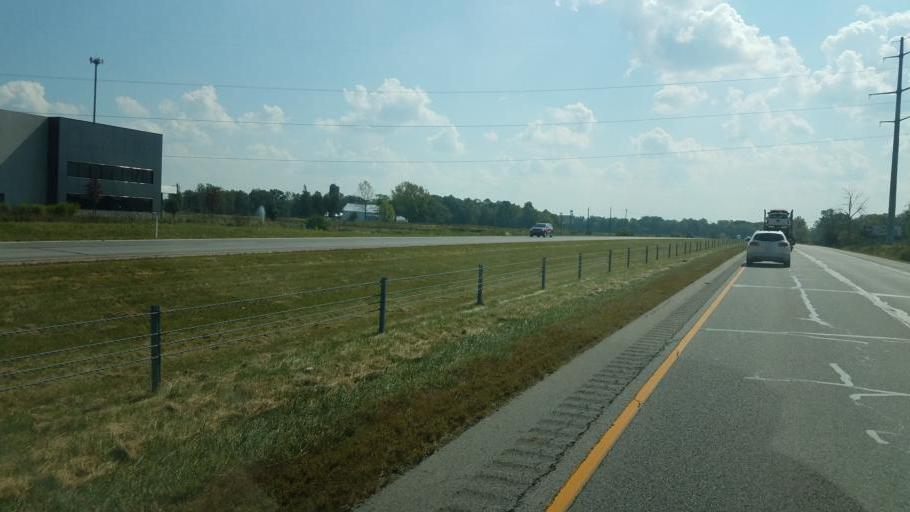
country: US
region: Indiana
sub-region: Allen County
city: Leo-Cedarville
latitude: 41.2678
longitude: -85.0869
